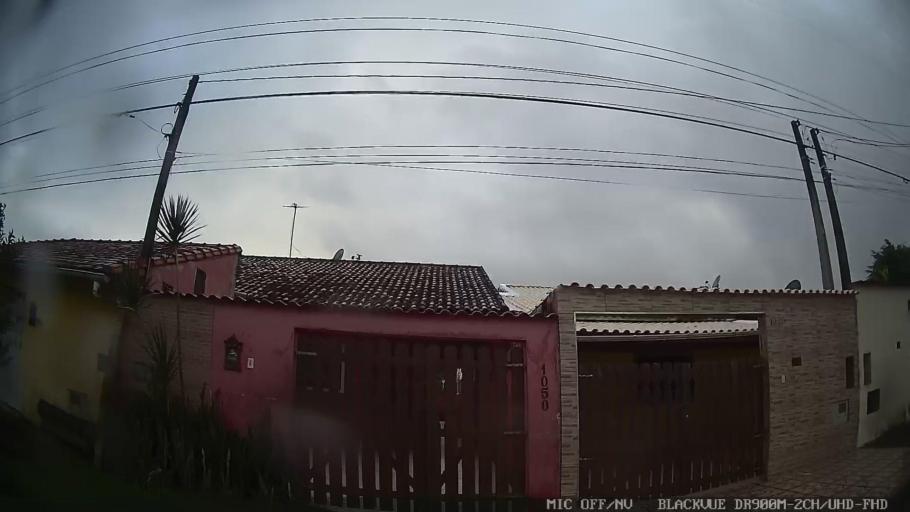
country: BR
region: Sao Paulo
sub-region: Itanhaem
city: Itanhaem
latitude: -24.1664
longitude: -46.7707
